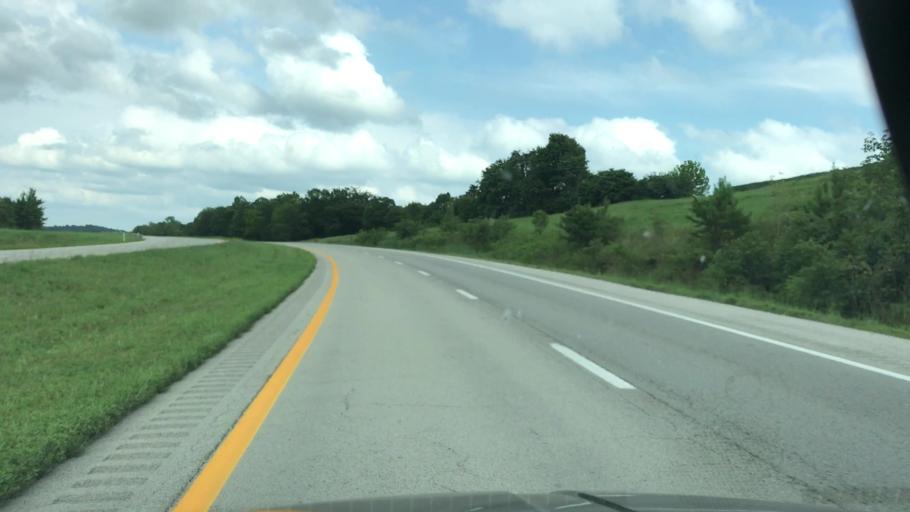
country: US
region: Kentucky
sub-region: Caldwell County
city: Princeton
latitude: 37.1403
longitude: -87.8165
